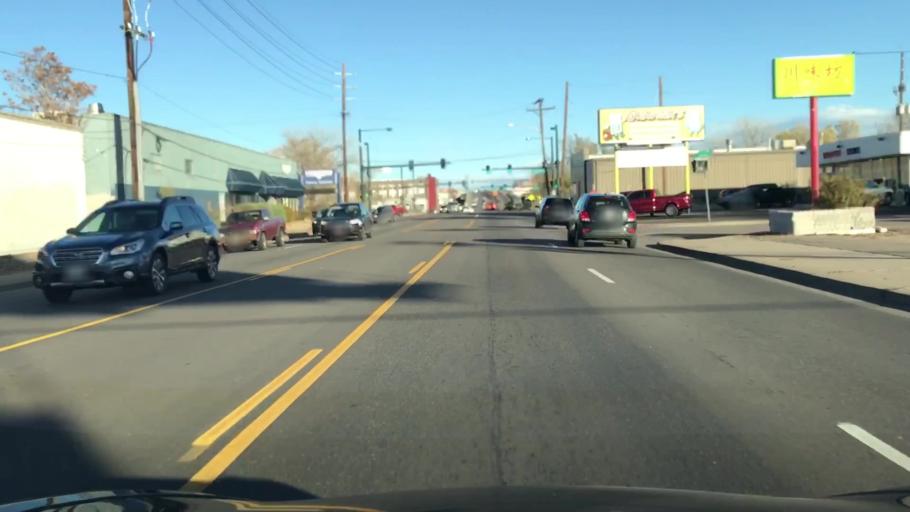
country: US
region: Colorado
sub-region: Arapahoe County
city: Englewood
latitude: 39.6785
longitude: -104.9999
